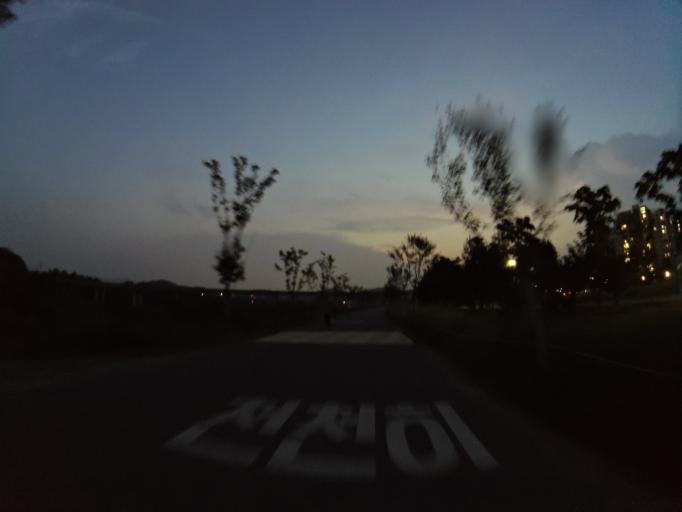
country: KR
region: Gyeongsangbuk-do
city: Gyeongsan-si
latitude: 35.8589
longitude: 128.6910
